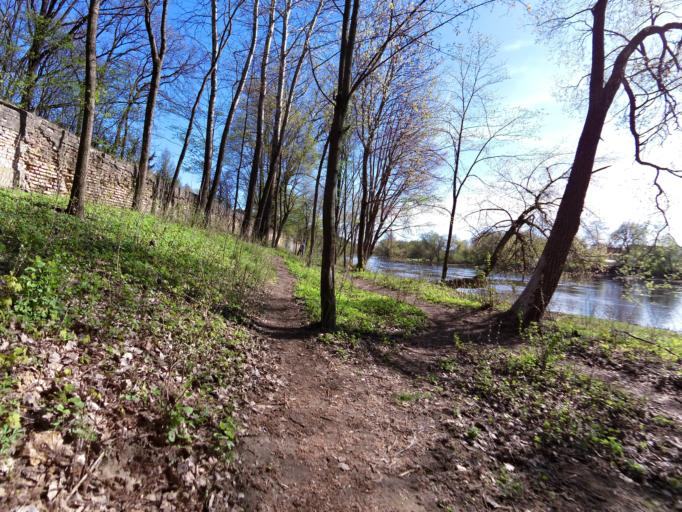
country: LT
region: Vilnius County
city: Vilkpede
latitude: 54.6829
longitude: 25.2302
